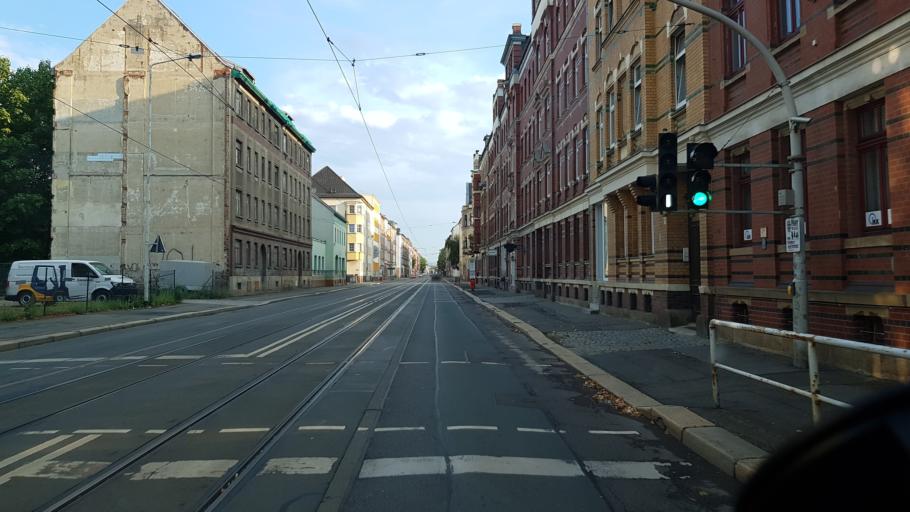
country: DE
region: Saxony
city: Zwickau
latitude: 50.7342
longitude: 12.4910
